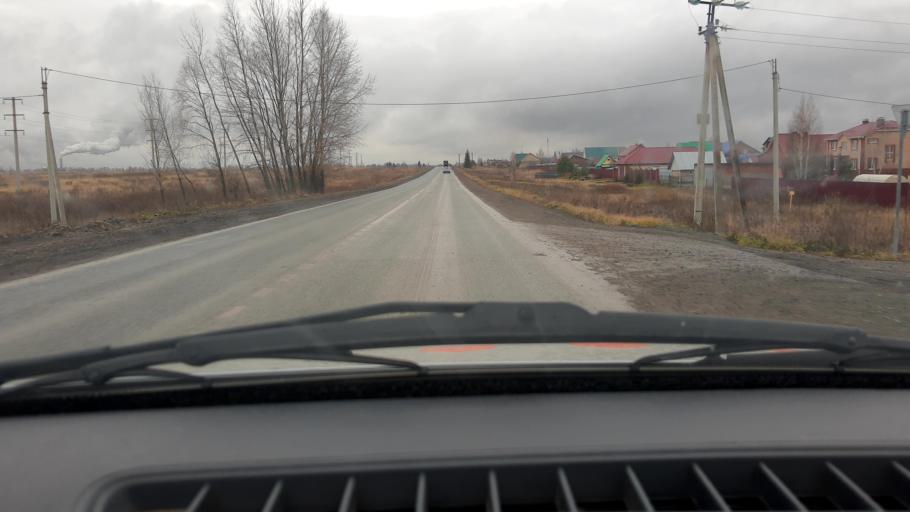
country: RU
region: Bashkortostan
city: Iglino
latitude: 54.7850
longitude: 56.2526
